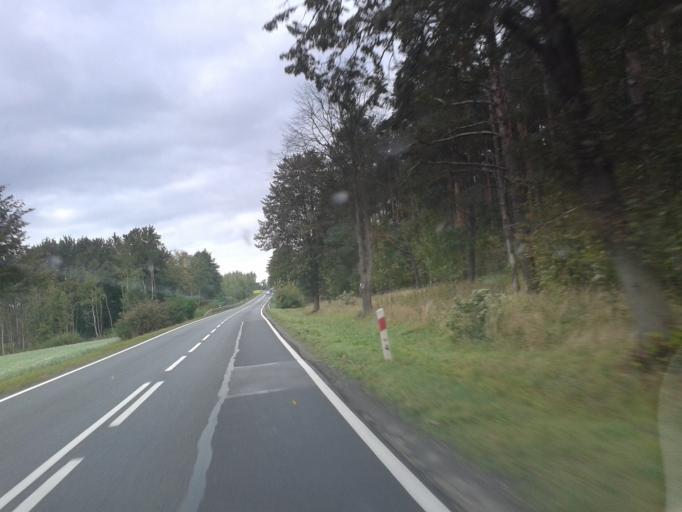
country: PL
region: Kujawsko-Pomorskie
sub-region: Powiat sepolenski
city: Sepolno Krajenskie
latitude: 53.4791
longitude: 17.5223
